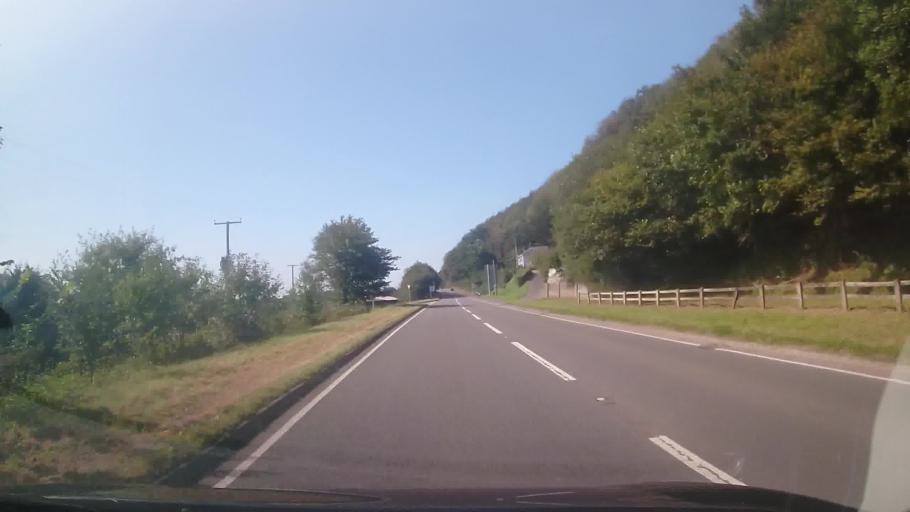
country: GB
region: Wales
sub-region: Carmarthenshire
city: Carmarthen
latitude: 51.8684
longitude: -4.2395
